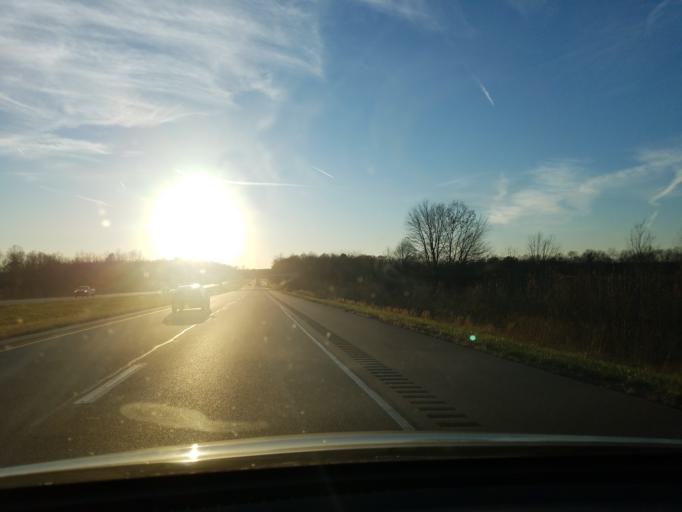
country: US
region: Indiana
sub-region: Warrick County
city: Chandler
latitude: 38.1885
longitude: -87.3528
